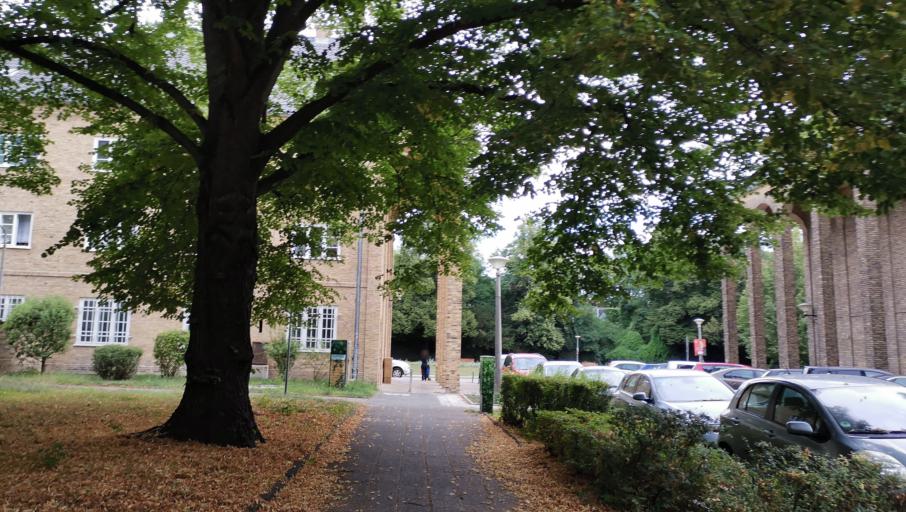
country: DE
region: Brandenburg
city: Potsdam
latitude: 52.3917
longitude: 13.0374
